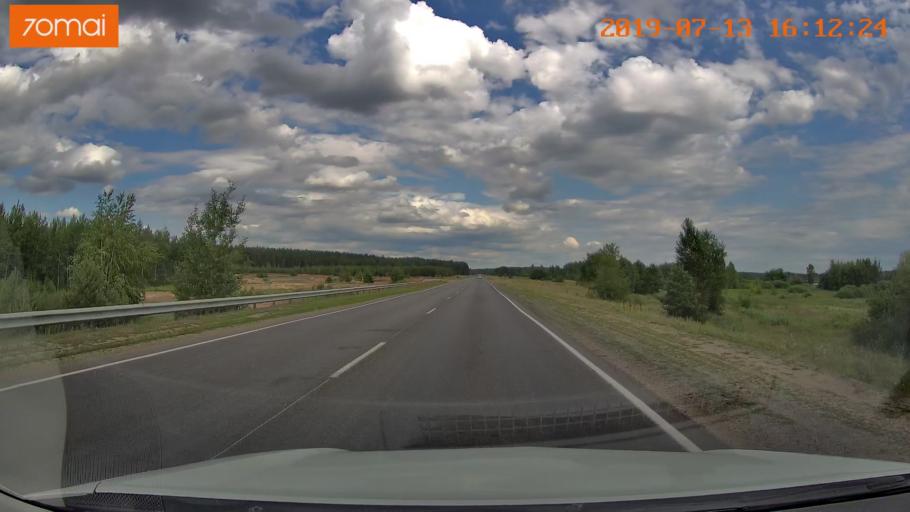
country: BY
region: Mogilev
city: Babruysk
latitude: 53.1672
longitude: 29.2793
